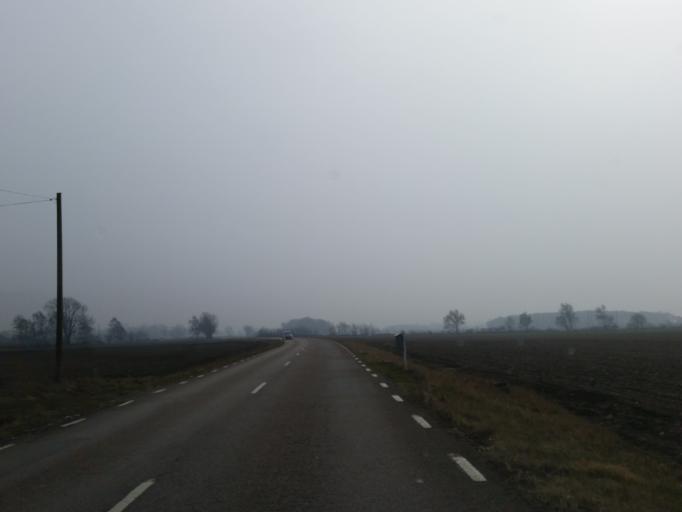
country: SE
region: Kalmar
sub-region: Morbylanga Kommun
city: Moerbylanga
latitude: 56.4143
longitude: 16.4135
